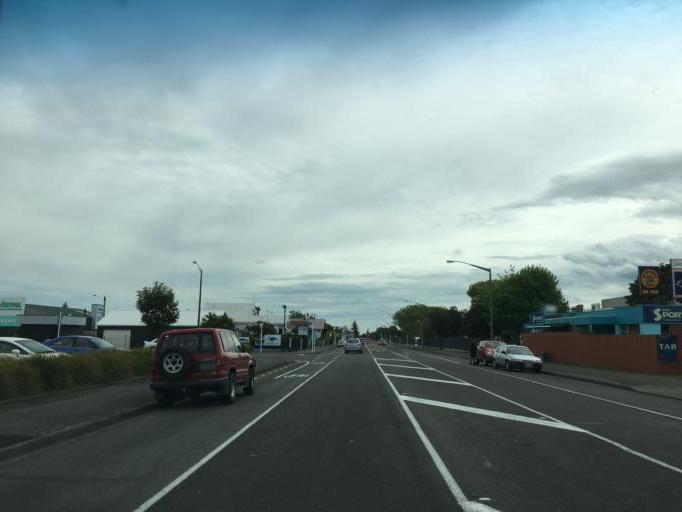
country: NZ
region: Manawatu-Wanganui
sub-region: Palmerston North City
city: Palmerston North
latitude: -40.3504
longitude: 175.6052
